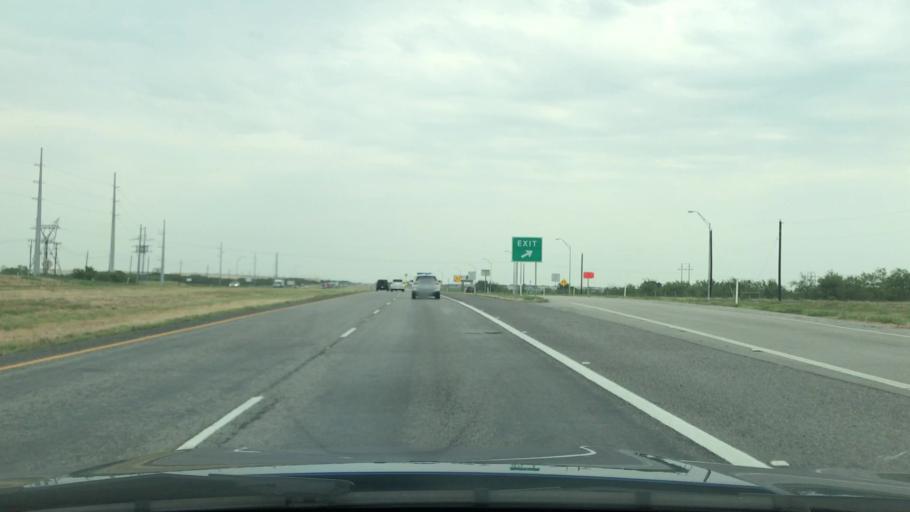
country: US
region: Texas
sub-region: Kaufman County
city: Terrell
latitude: 32.7291
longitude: -96.3390
